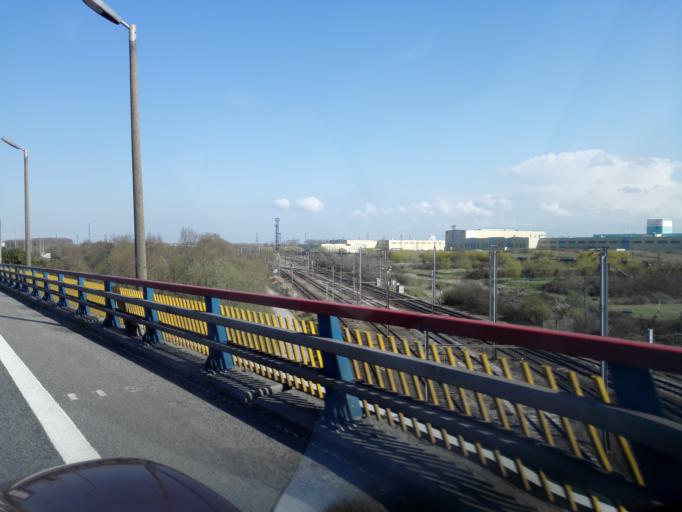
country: FR
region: Nord-Pas-de-Calais
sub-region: Departement du Nord
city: Grande-Synthe
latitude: 50.9934
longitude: 2.2737
